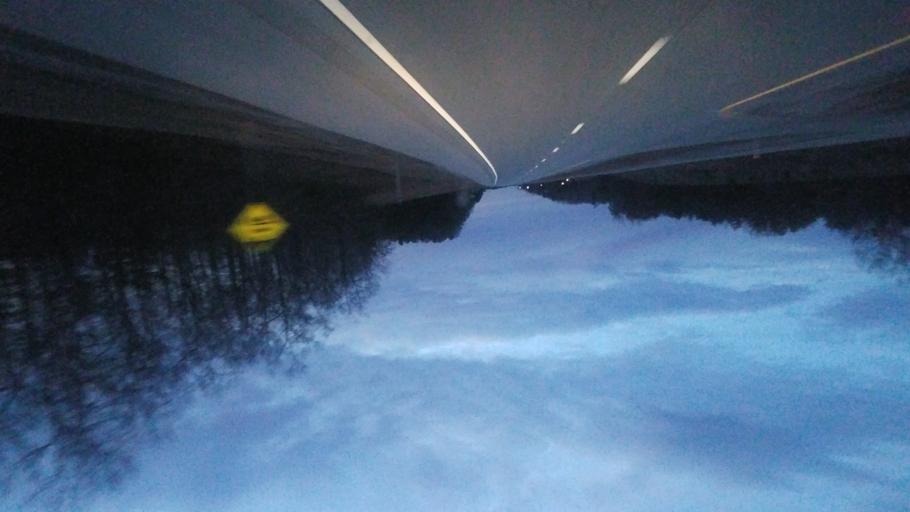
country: US
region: Tennessee
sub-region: Van Buren County
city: Spencer
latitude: 35.5830
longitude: -85.4716
